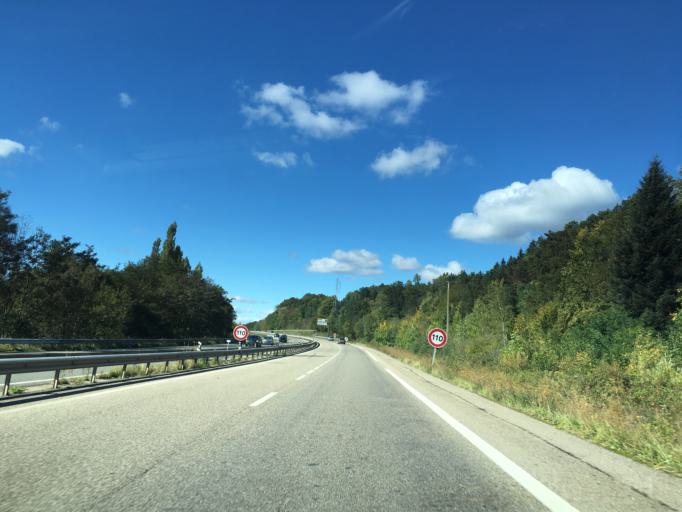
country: FR
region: Lorraine
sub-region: Departement des Vosges
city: Etival-Clairefontaine
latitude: 48.3890
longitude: 6.8645
